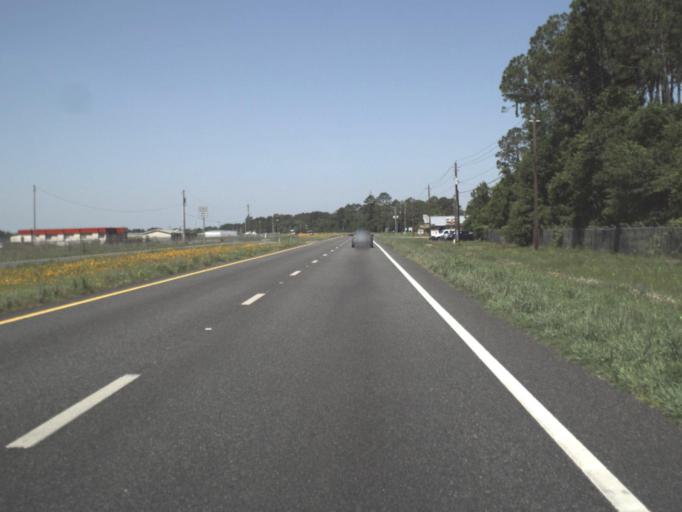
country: US
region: Florida
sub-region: Columbia County
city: Watertown
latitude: 30.1886
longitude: -82.5724
